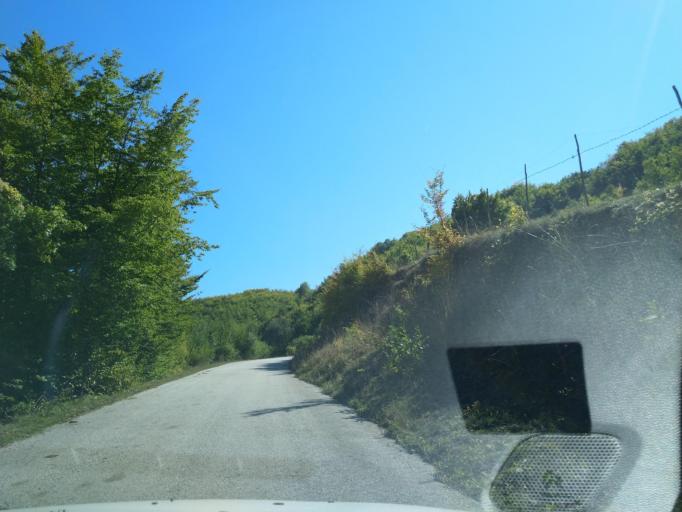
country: RS
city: Sokolovica
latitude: 43.2578
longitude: 20.3017
